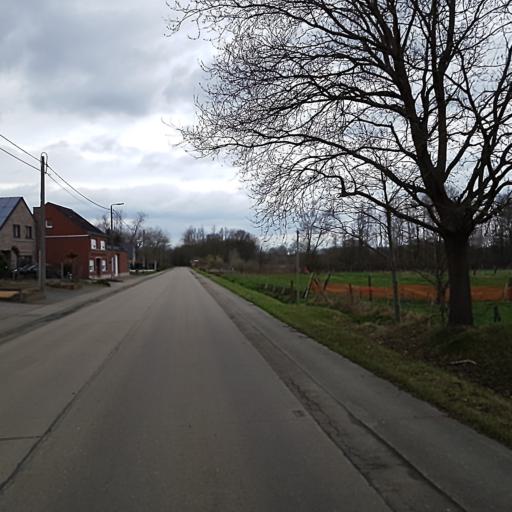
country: BE
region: Flanders
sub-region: Provincie Vlaams-Brabant
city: Begijnendijk
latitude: 50.9719
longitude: 4.7792
